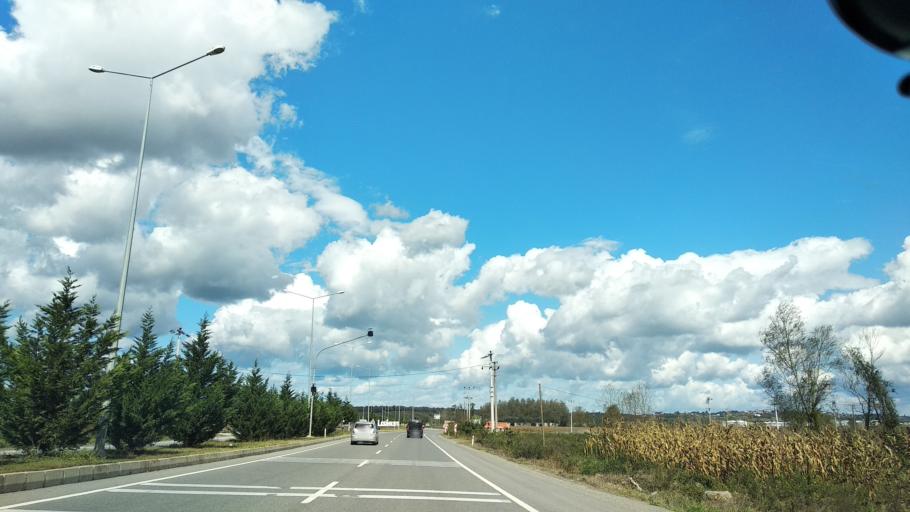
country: TR
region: Sakarya
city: Ferizli
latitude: 40.9564
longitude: 30.5061
